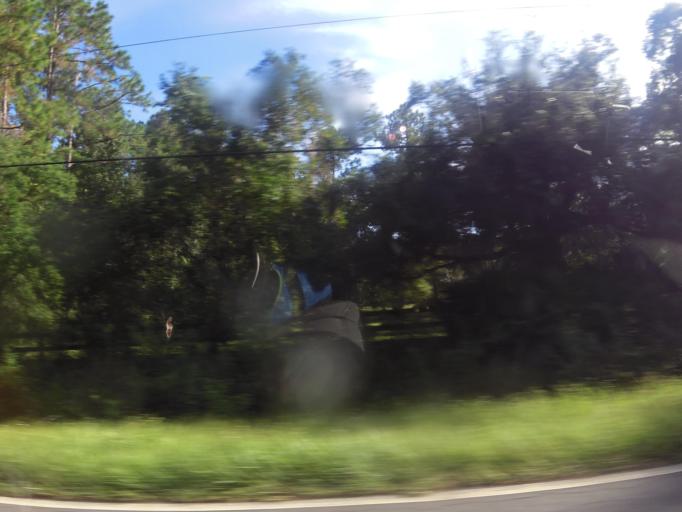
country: US
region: Florida
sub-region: Clay County
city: Green Cove Springs
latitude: 29.9157
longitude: -81.5885
